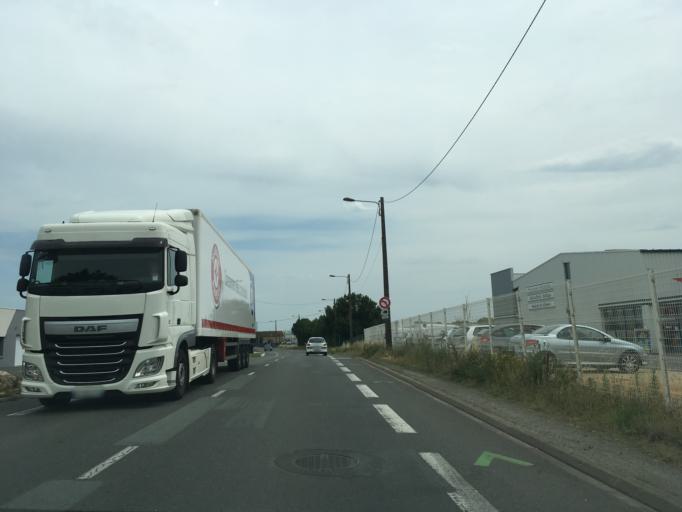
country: FR
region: Poitou-Charentes
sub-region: Departement des Deux-Sevres
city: Bessines
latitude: 46.3132
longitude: -0.4978
